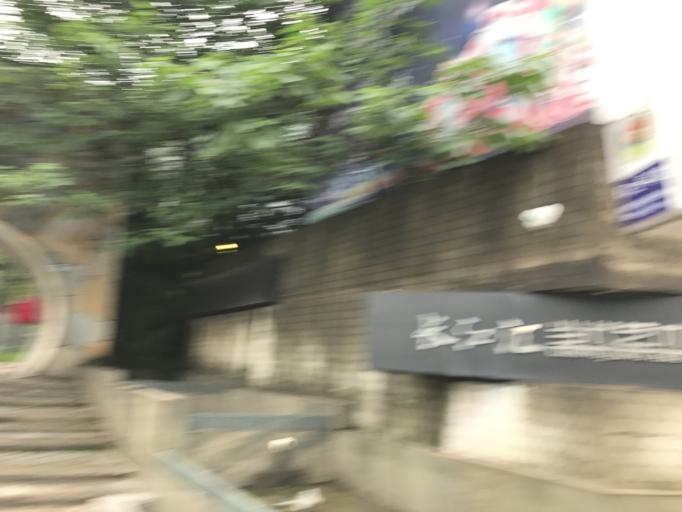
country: CN
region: Chongqing Shi
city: Nanping
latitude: 29.5608
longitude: 106.5909
